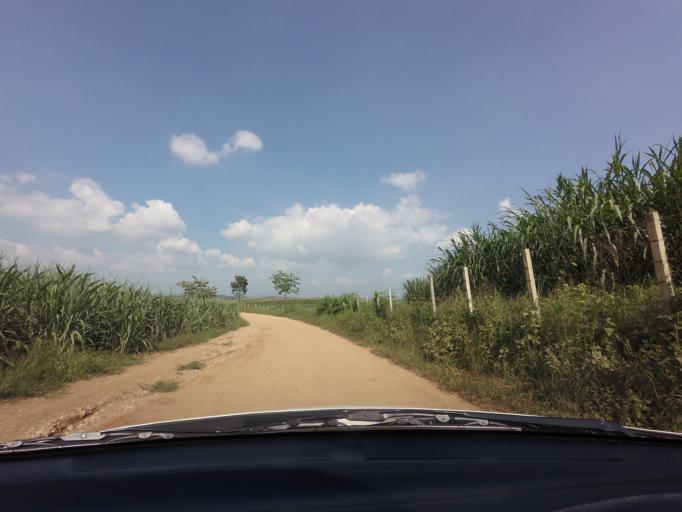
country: TH
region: Nakhon Ratchasima
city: Wang Nam Khiao
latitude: 14.4964
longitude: 101.6301
